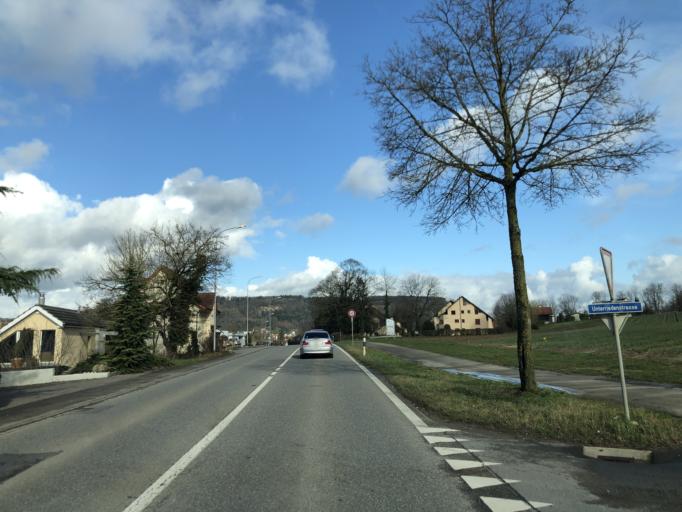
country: CH
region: Aargau
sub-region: Bezirk Baden
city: Gebenstorf
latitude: 47.4747
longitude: 8.2320
